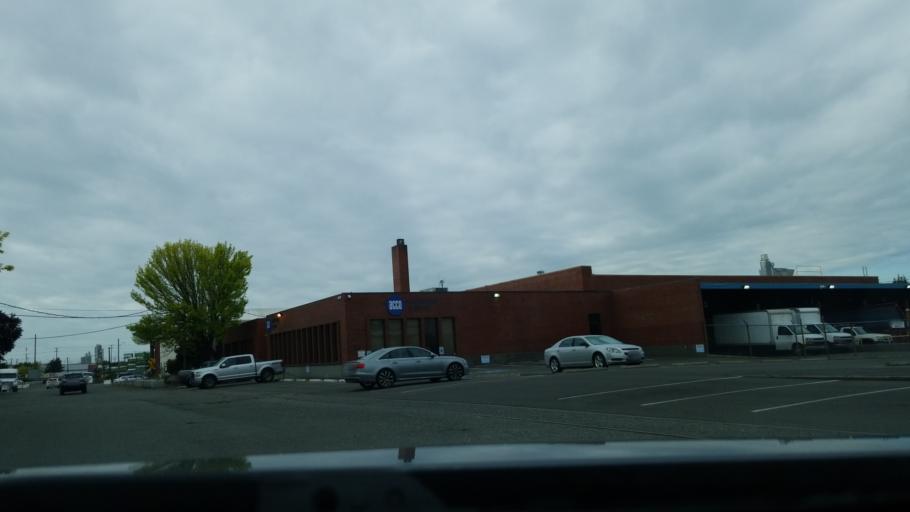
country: US
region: Washington
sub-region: King County
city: White Center
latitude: 47.5542
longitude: -122.3249
